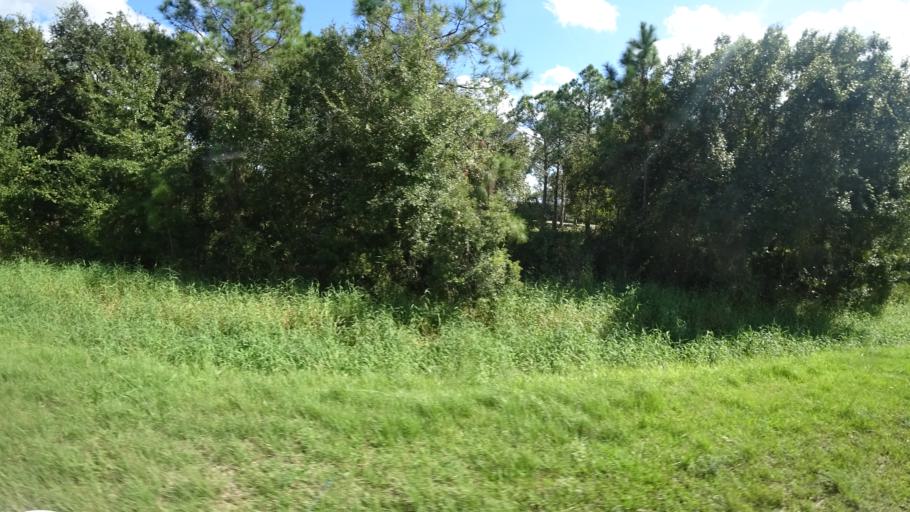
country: US
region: Florida
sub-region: Sarasota County
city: Lake Sarasota
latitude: 27.3855
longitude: -82.1384
